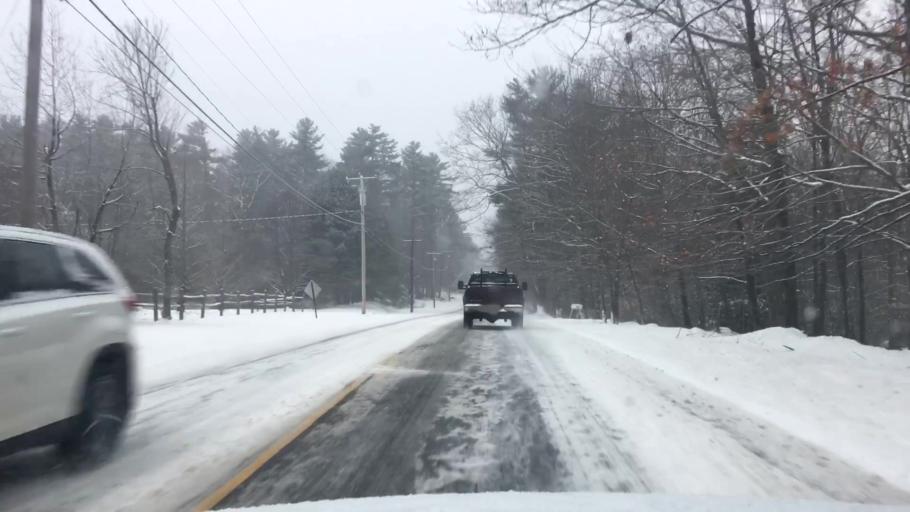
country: US
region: Maine
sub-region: Cumberland County
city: Cumberland Center
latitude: 43.8273
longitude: -70.3174
